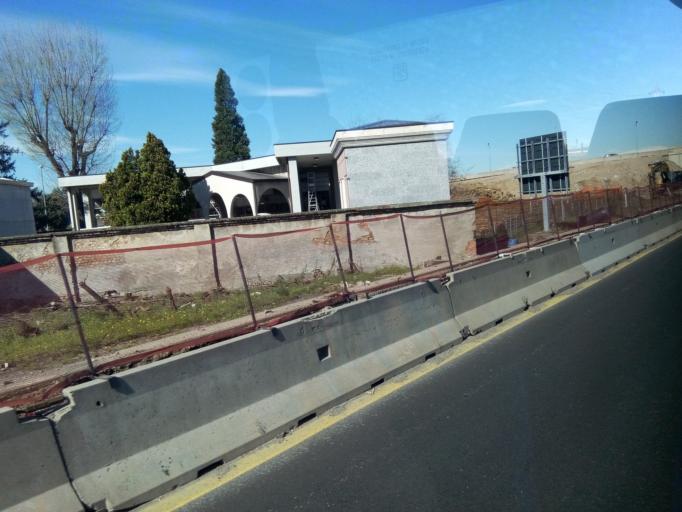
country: IT
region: Lombardy
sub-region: Citta metropolitana di Milano
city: Passirana
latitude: 45.5516
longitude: 9.0536
